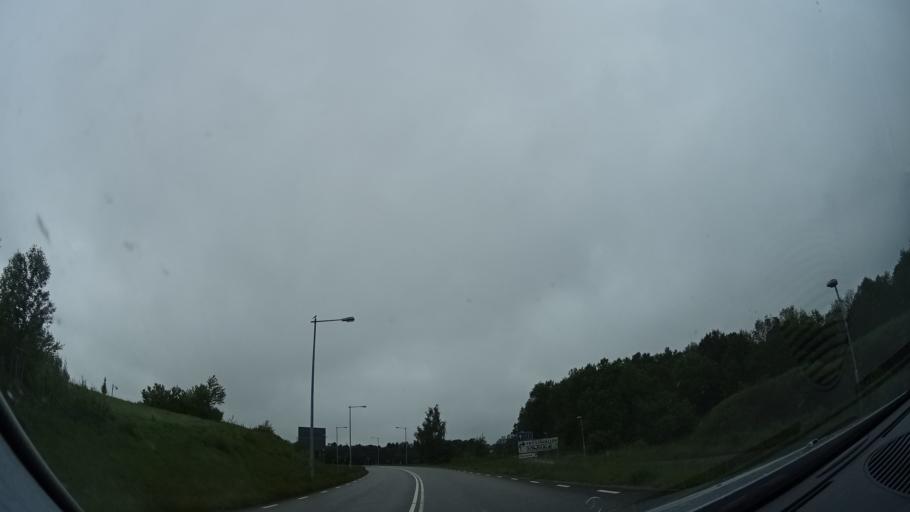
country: SE
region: Skane
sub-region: Hoors Kommun
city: Hoeoer
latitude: 55.9447
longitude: 13.5410
